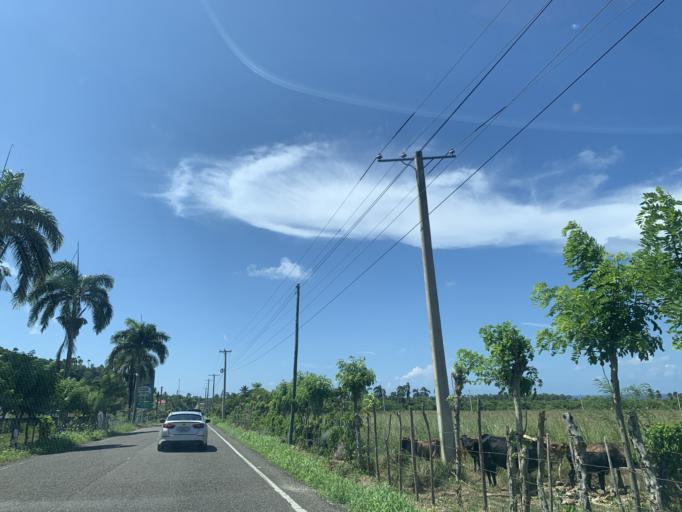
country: DO
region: Maria Trinidad Sanchez
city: Cabrera
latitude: 19.6656
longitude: -69.9455
